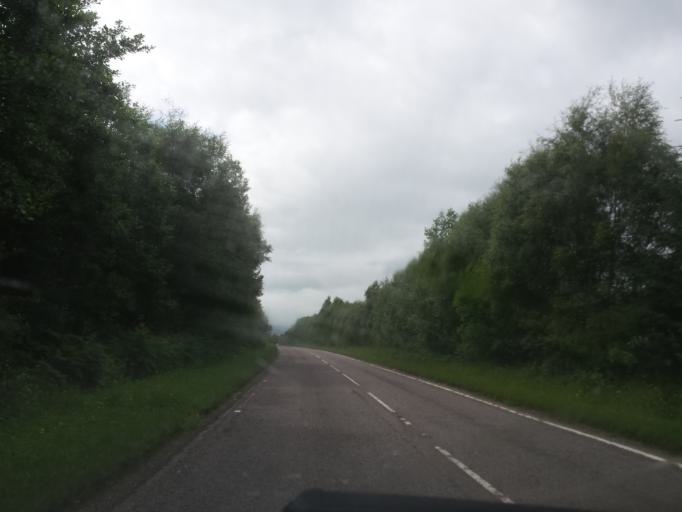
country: GB
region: Scotland
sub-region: Highland
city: Fort William
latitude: 56.8564
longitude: -5.2937
